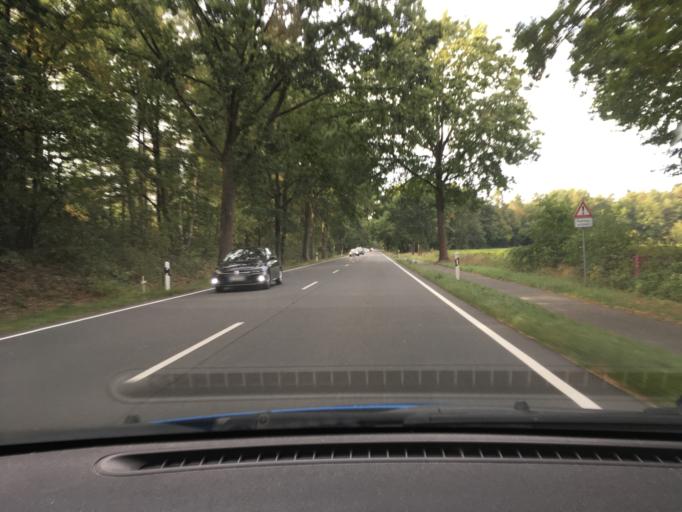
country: DE
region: Lower Saxony
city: Wietzendorf
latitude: 52.9067
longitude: 9.9177
